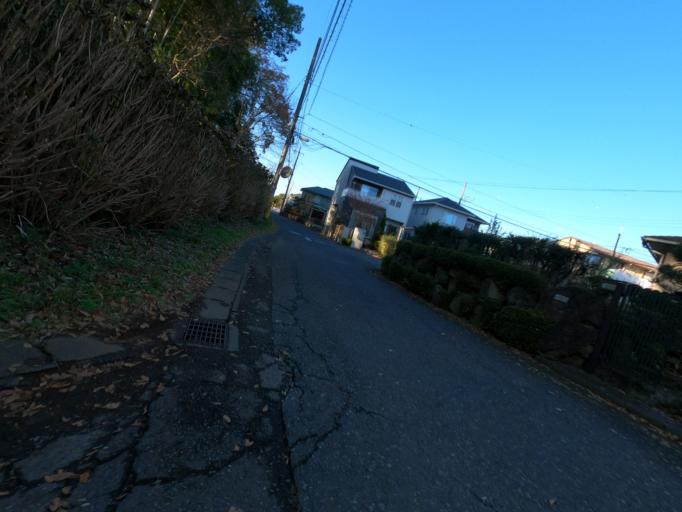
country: JP
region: Ibaraki
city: Moriya
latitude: 35.9306
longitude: 139.9984
